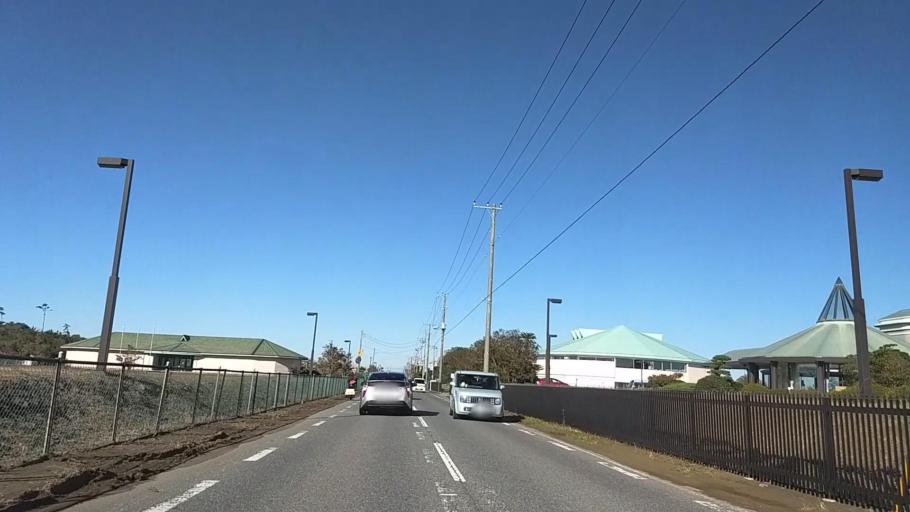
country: JP
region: Chiba
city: Mobara
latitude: 35.3636
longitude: 140.3879
